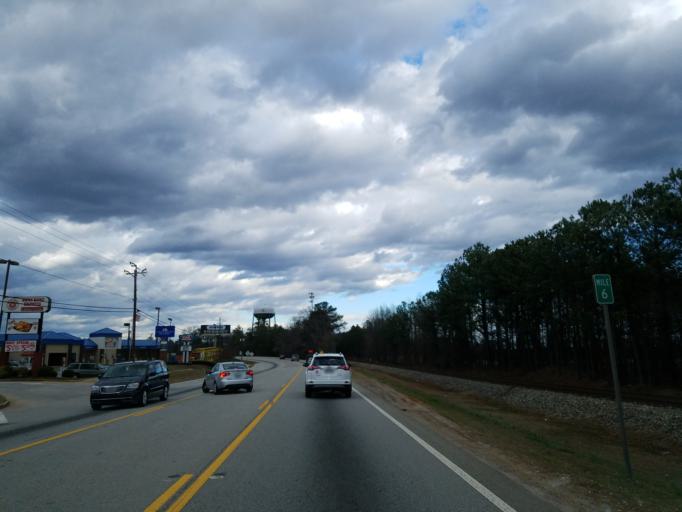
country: US
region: Georgia
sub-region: Henry County
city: McDonough
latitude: 33.4144
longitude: -84.1560
